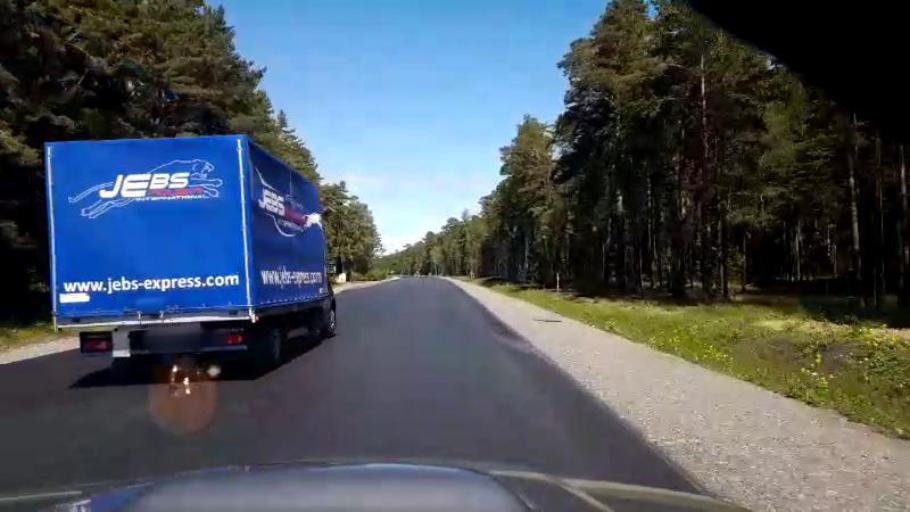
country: LV
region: Salacgrivas
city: Ainazi
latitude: 57.8199
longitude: 24.3470
